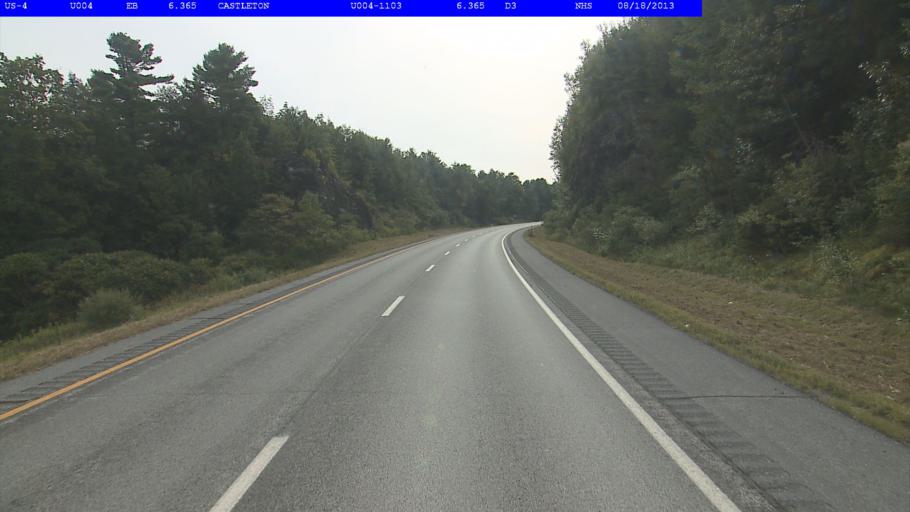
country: US
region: Vermont
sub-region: Rutland County
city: Castleton
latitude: 43.6227
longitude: -73.1913
